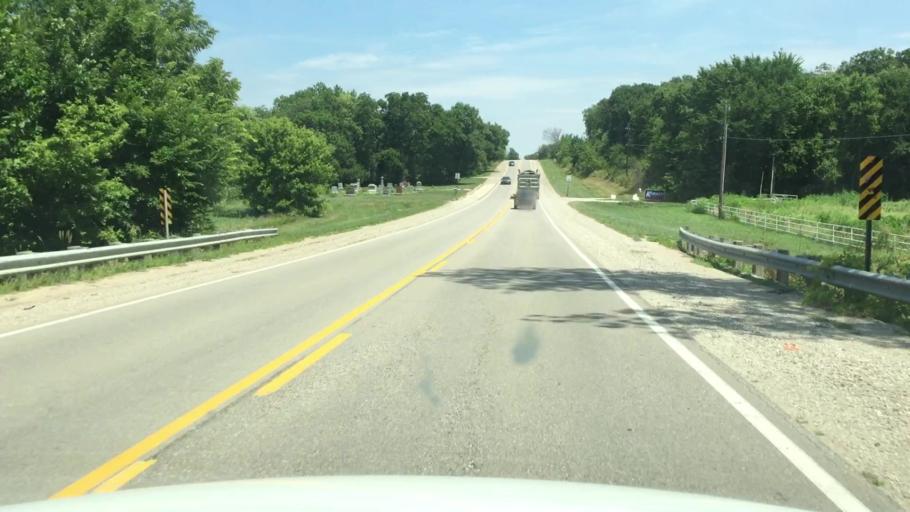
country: US
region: Kansas
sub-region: Shawnee County
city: Topeka
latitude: 38.9861
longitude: -95.5782
